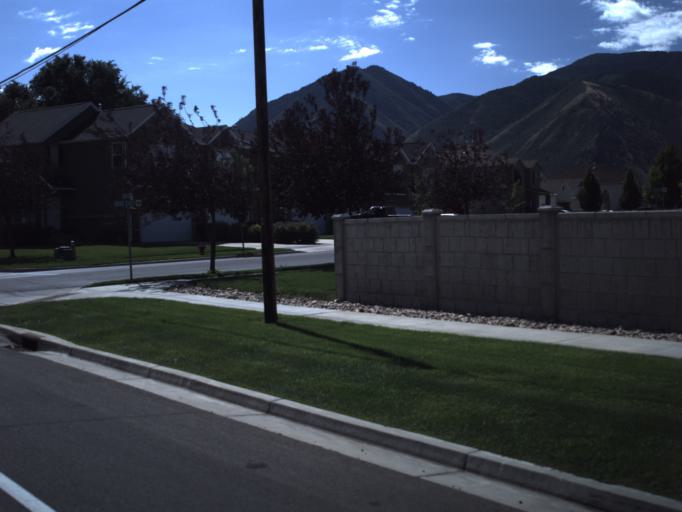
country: US
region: Utah
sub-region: Utah County
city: Spanish Fork
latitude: 40.0982
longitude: -111.6239
